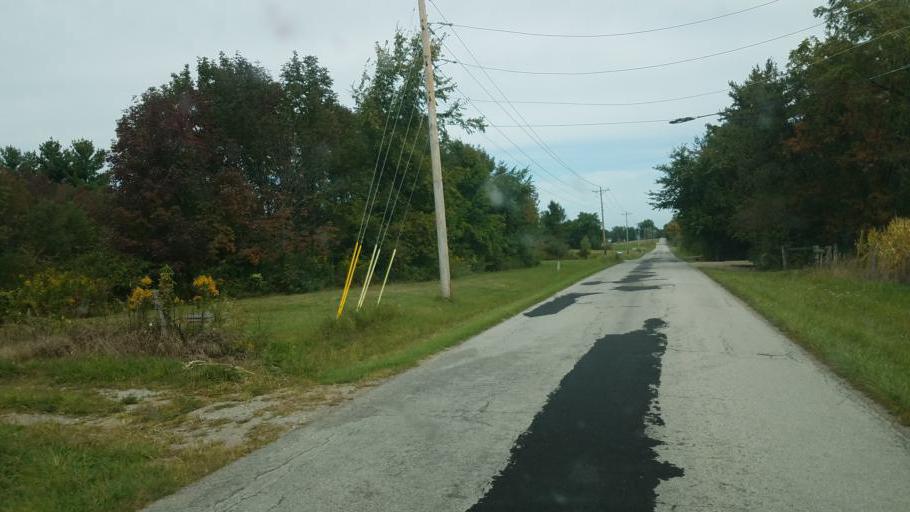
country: US
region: Ohio
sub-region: Knox County
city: Centerburg
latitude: 40.3542
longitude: -82.7254
